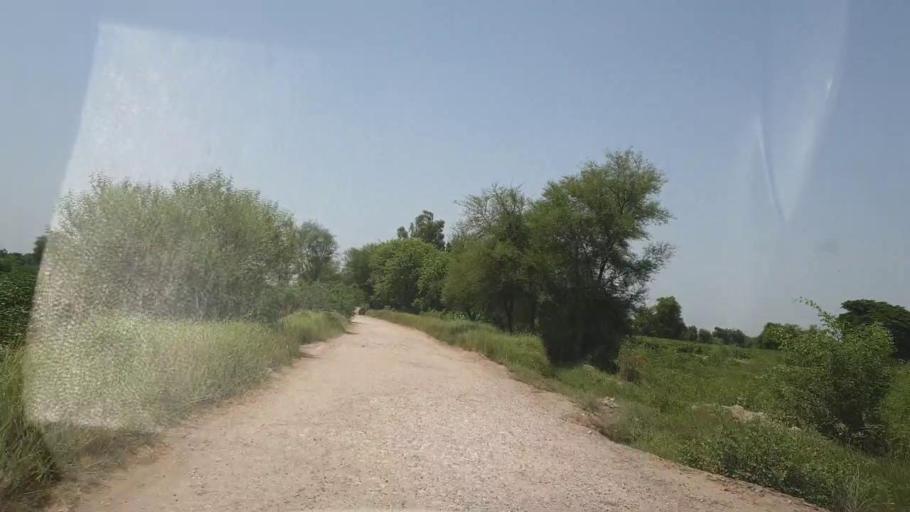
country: PK
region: Sindh
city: Bozdar
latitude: 27.1285
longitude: 68.6269
